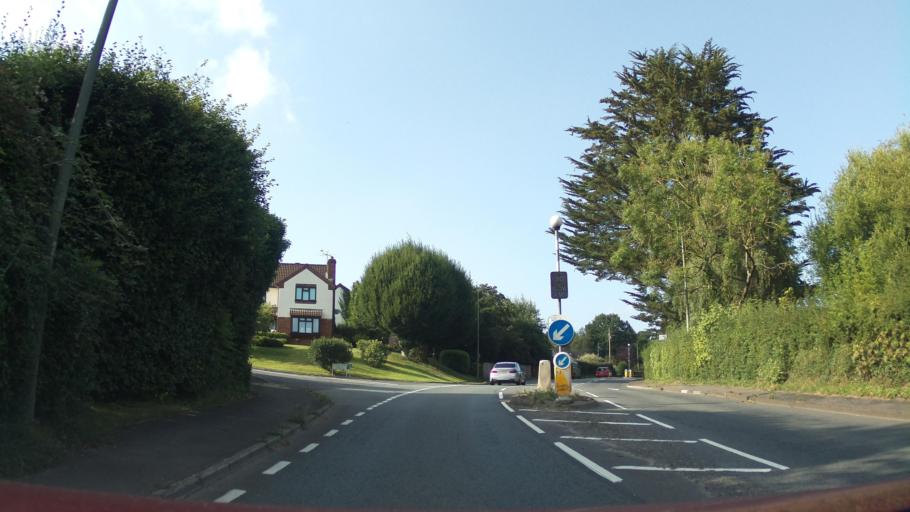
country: GB
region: England
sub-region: Devon
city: Tiverton
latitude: 50.8900
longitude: -3.4969
